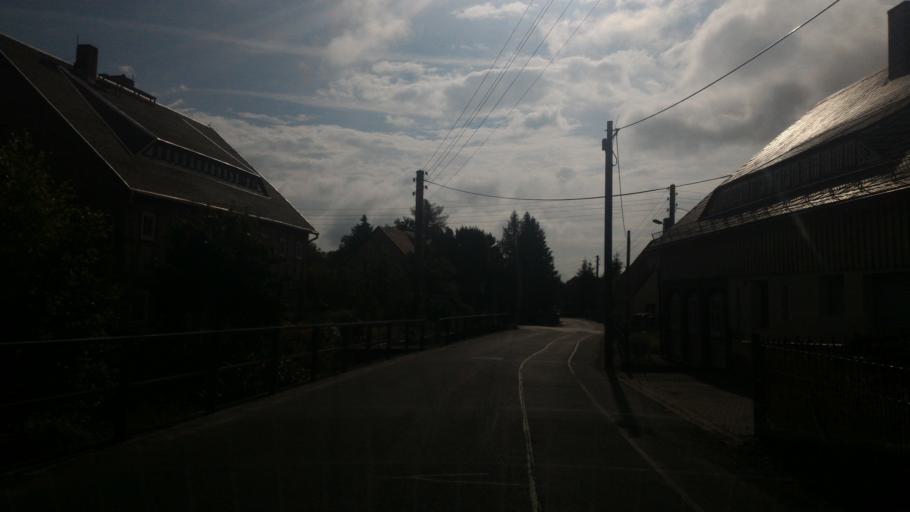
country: DE
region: Saxony
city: Hainewalde
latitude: 50.9384
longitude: 14.6871
